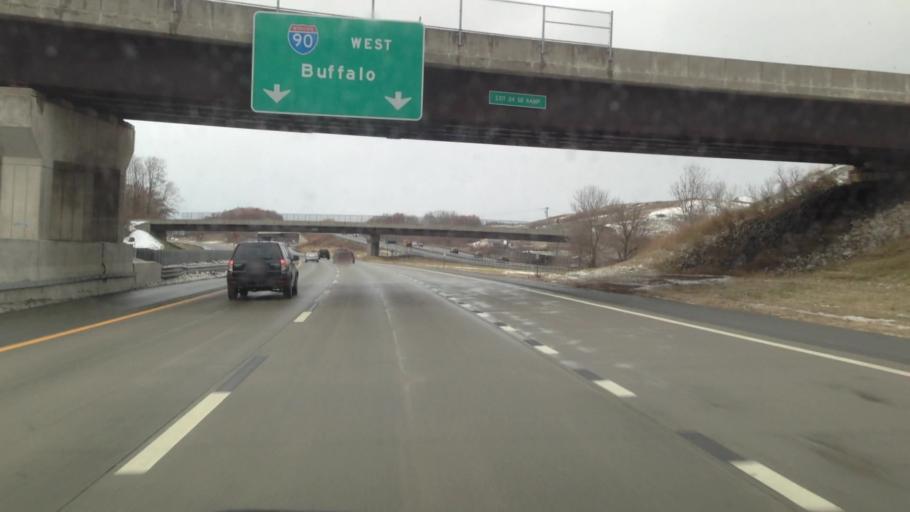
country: US
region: New York
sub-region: Albany County
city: McKownville
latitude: 42.7013
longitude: -73.8484
